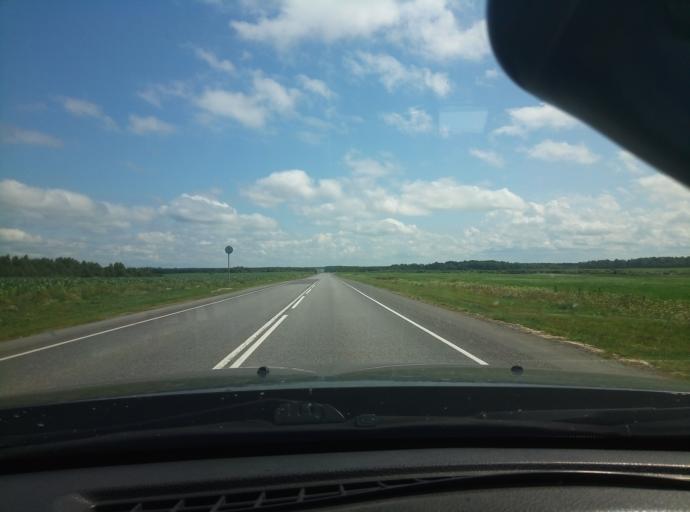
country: RU
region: Tula
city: Khanino
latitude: 54.4059
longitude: 36.5634
